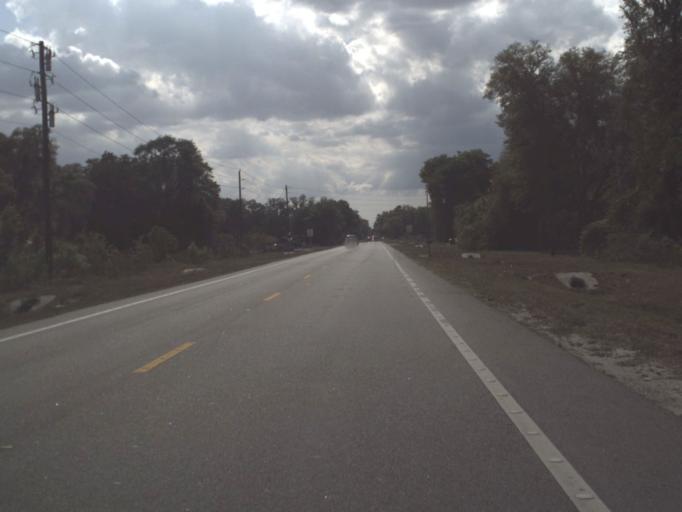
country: US
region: Florida
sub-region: Hernando County
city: Ridge Manor
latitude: 28.5552
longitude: -82.0609
